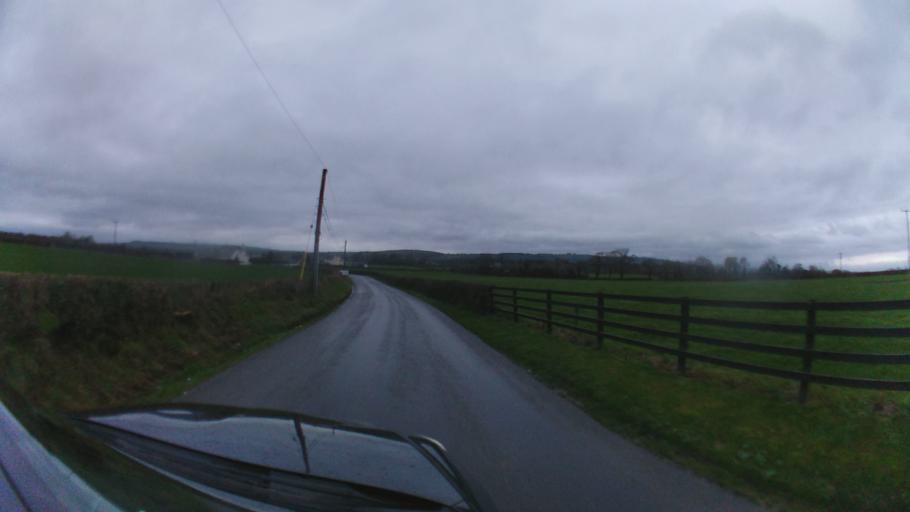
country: IE
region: Leinster
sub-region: County Carlow
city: Bagenalstown
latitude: 52.6779
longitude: -7.0152
